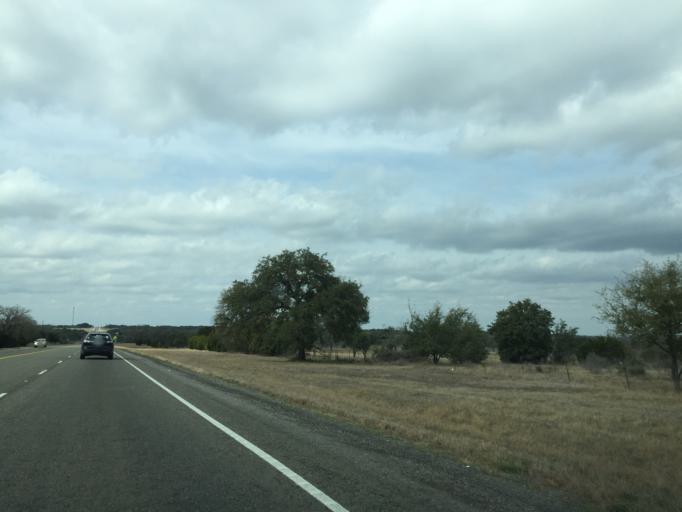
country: US
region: Texas
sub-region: Burnet County
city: Meadowlakes
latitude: 30.5046
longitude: -98.2778
